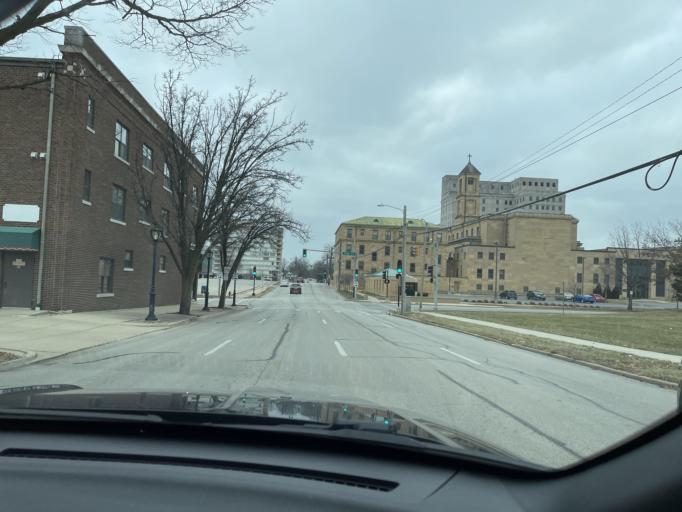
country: US
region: Illinois
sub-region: Sangamon County
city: Springfield
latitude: 39.7939
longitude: -89.6502
